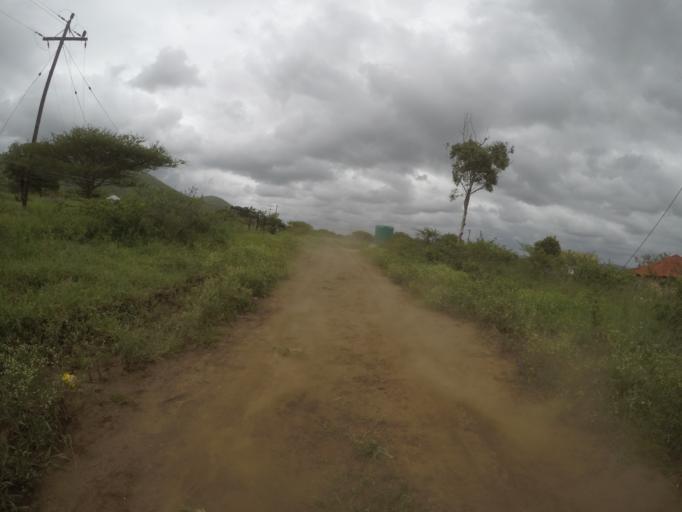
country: ZA
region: KwaZulu-Natal
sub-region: uThungulu District Municipality
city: Empangeni
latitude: -28.5609
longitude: 31.8784
